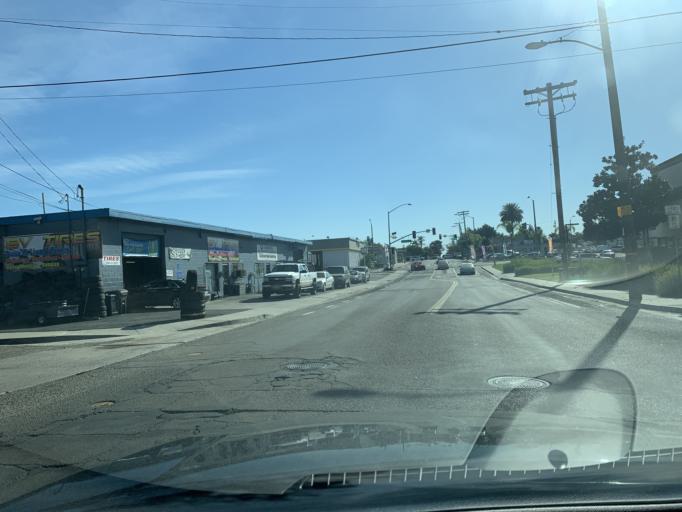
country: US
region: California
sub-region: San Diego County
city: Lemon Grove
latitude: 32.7437
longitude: -117.0342
